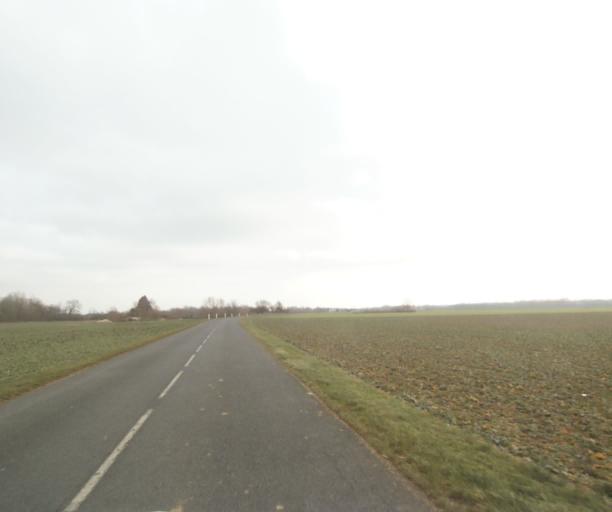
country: FR
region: Champagne-Ardenne
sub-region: Departement de la Haute-Marne
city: Villiers-en-Lieu
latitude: 48.6534
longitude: 4.7963
